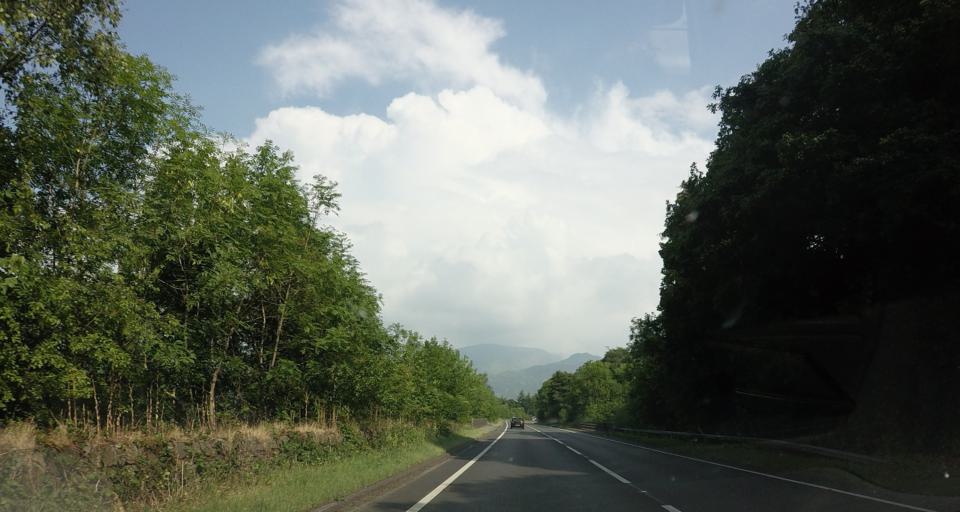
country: GB
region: England
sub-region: Cumbria
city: Cockermouth
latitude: 54.6666
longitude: -3.2376
